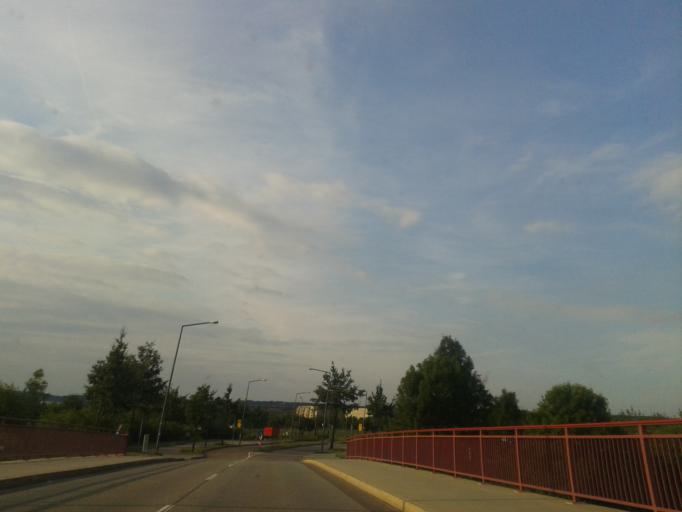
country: DE
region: Saxony
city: Dresden
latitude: 51.0759
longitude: 13.6990
